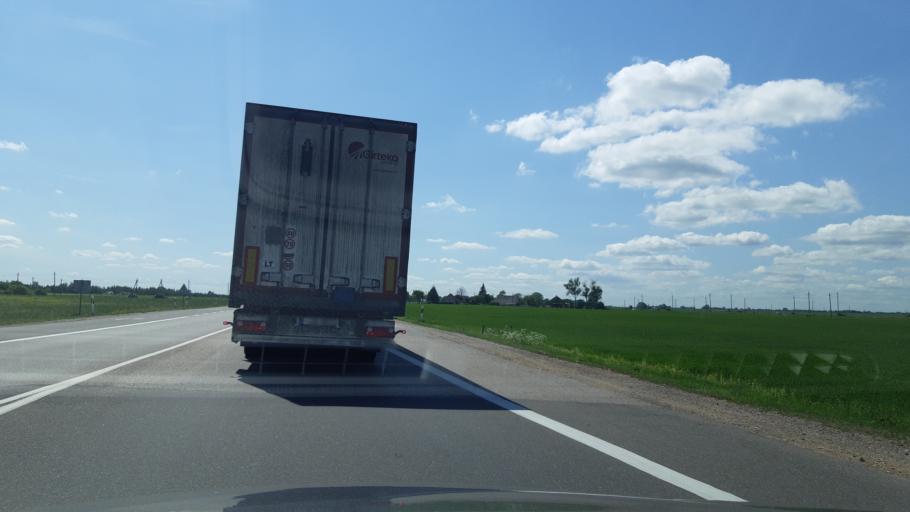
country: LT
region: Vilnius County
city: Ukmerge
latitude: 55.2698
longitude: 24.7631
